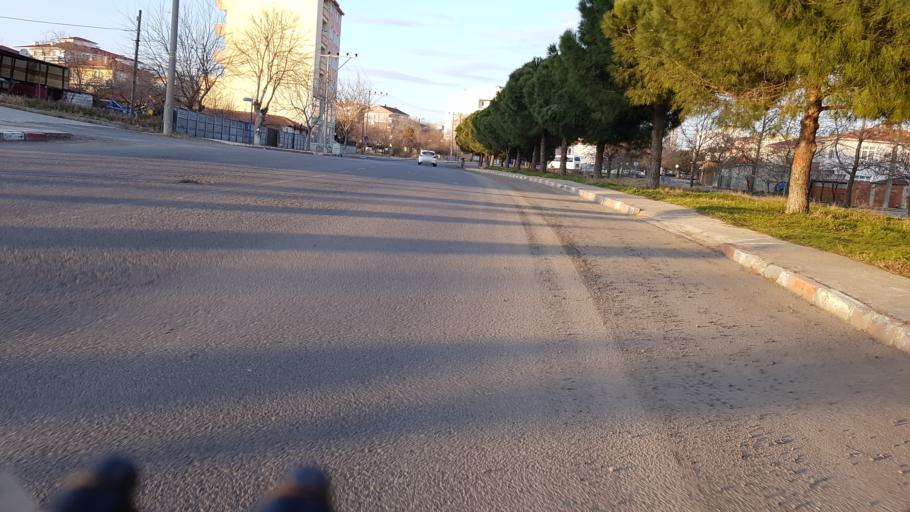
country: TR
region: Tekirdag
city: Velimese
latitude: 41.2508
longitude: 27.8747
